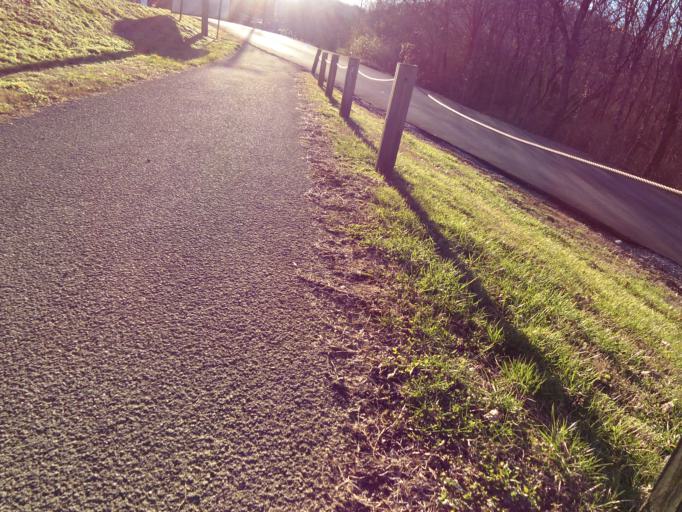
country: US
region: Tennessee
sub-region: Knox County
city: Knoxville
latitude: 35.9522
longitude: -83.8625
